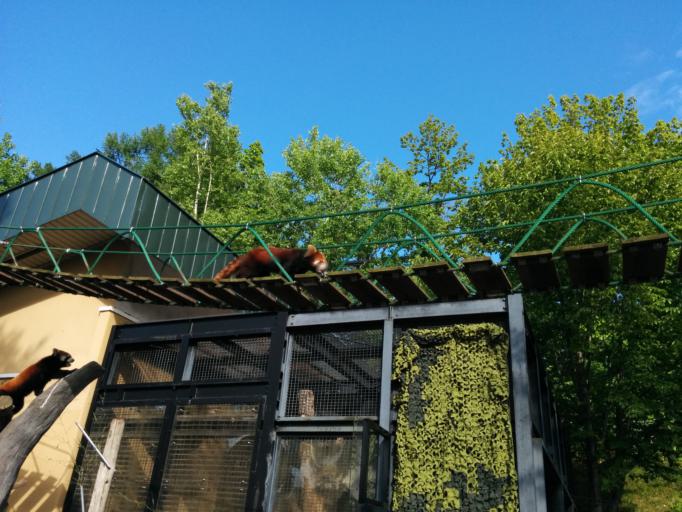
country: JP
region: Hokkaido
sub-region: Asahikawa-shi
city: Asahikawa
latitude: 43.7679
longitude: 142.4795
